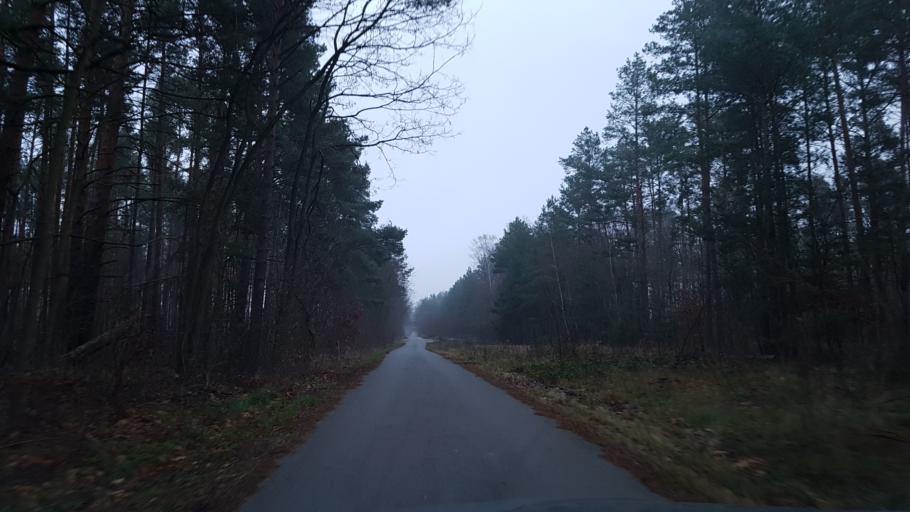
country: DE
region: Brandenburg
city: Ruckersdorf
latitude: 51.5448
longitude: 13.5797
